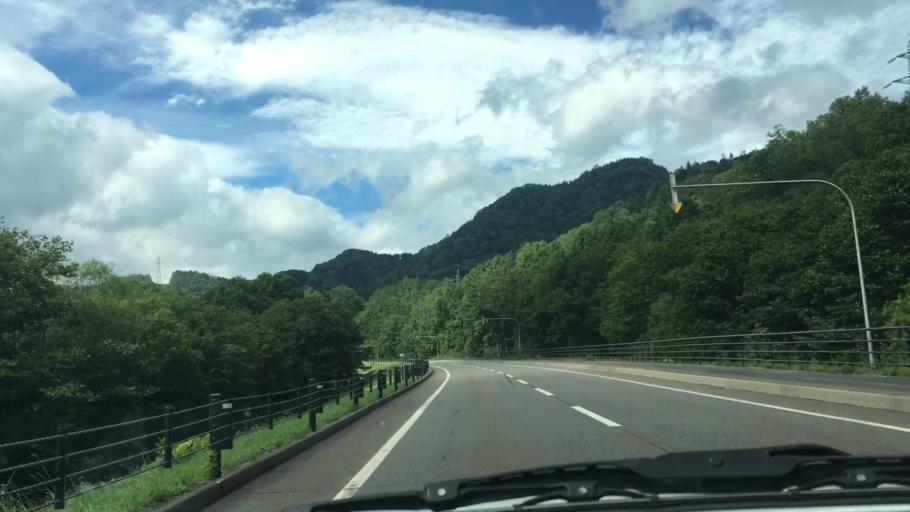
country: JP
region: Hokkaido
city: Otofuke
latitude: 43.3650
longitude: 143.2348
